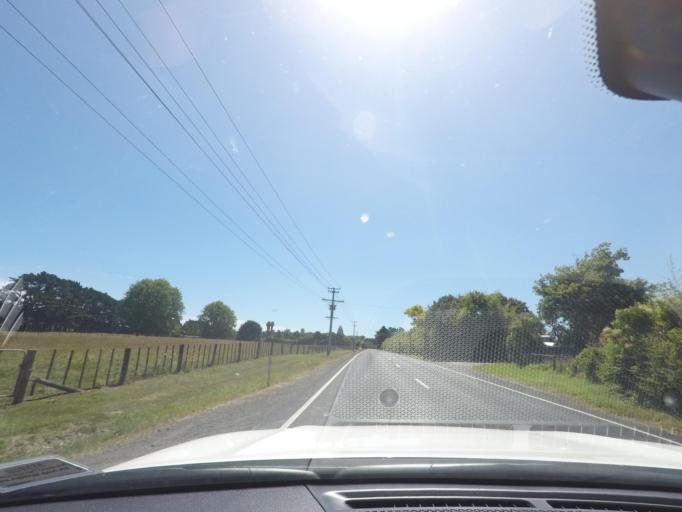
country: NZ
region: Auckland
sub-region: Auckland
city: Parakai
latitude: -36.6499
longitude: 174.4085
